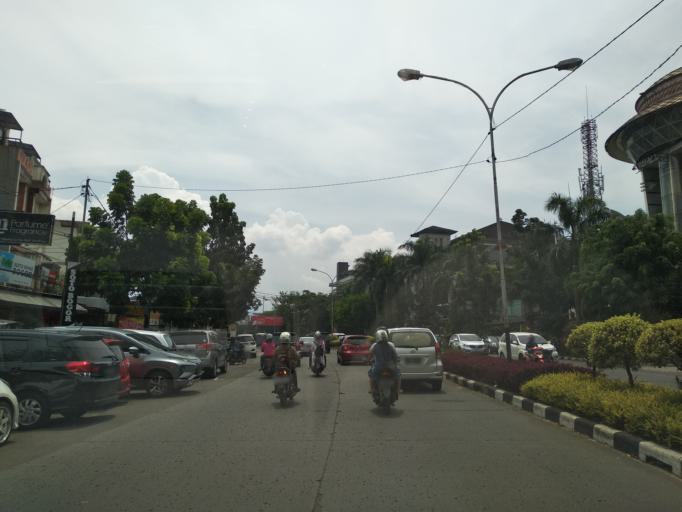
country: ID
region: West Java
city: Bandung
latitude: -6.9347
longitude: 107.6250
